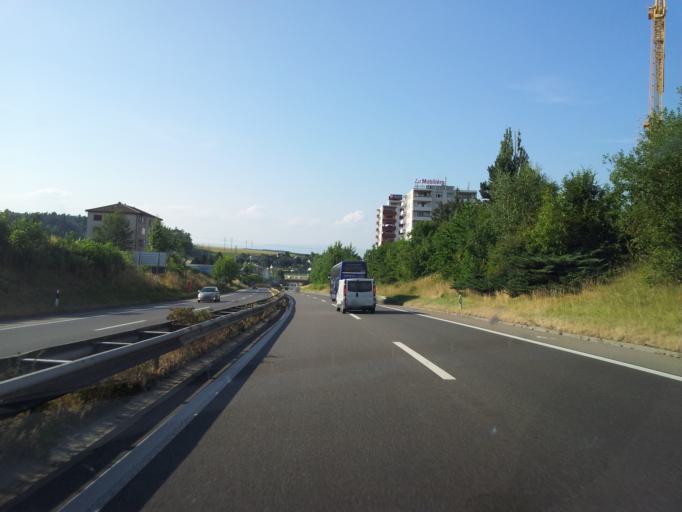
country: CH
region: Fribourg
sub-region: Sarine District
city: Givisiez
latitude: 46.8131
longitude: 7.1388
